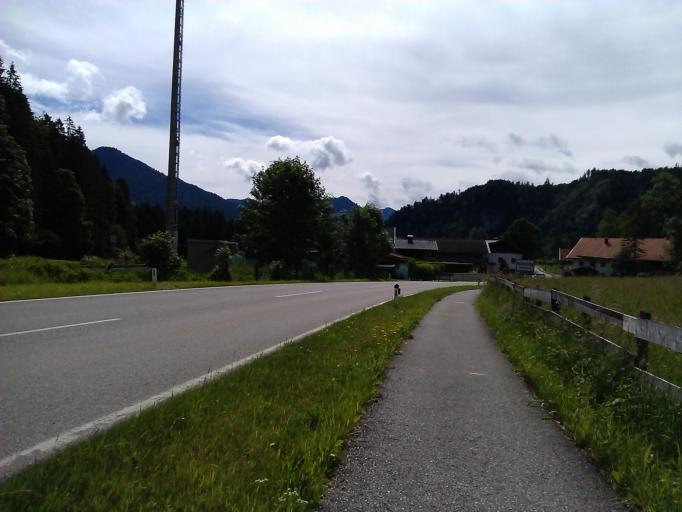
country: AT
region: Tyrol
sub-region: Politischer Bezirk Reutte
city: Musau
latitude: 47.5206
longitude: 10.6849
